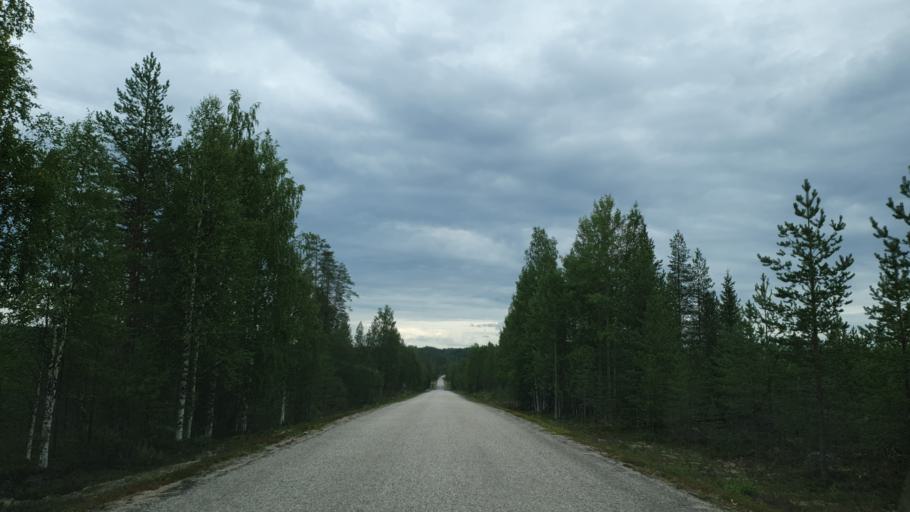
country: FI
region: Kainuu
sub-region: Kehys-Kainuu
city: Kuhmo
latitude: 64.3404
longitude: 29.3170
